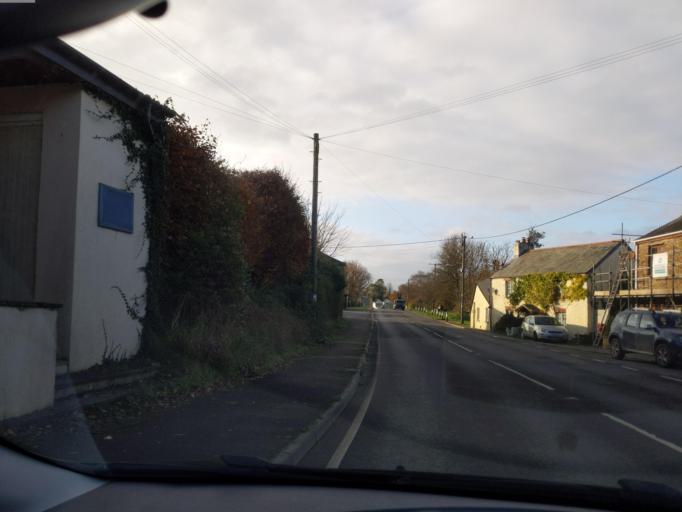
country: GB
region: England
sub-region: Cornwall
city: Wadebridge
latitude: 50.5090
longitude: -4.8054
